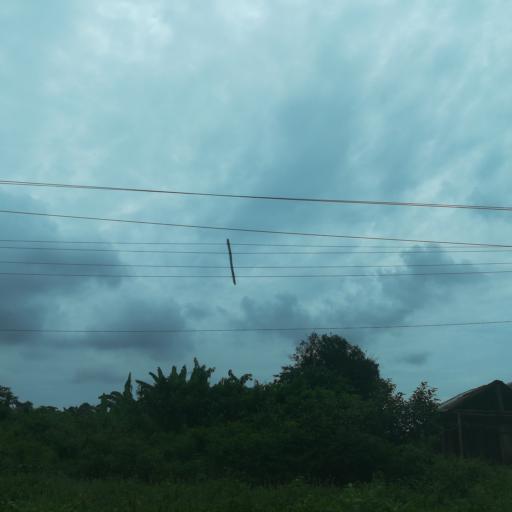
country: NG
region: Ogun
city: Odogbolu
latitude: 6.6754
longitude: 3.7124
